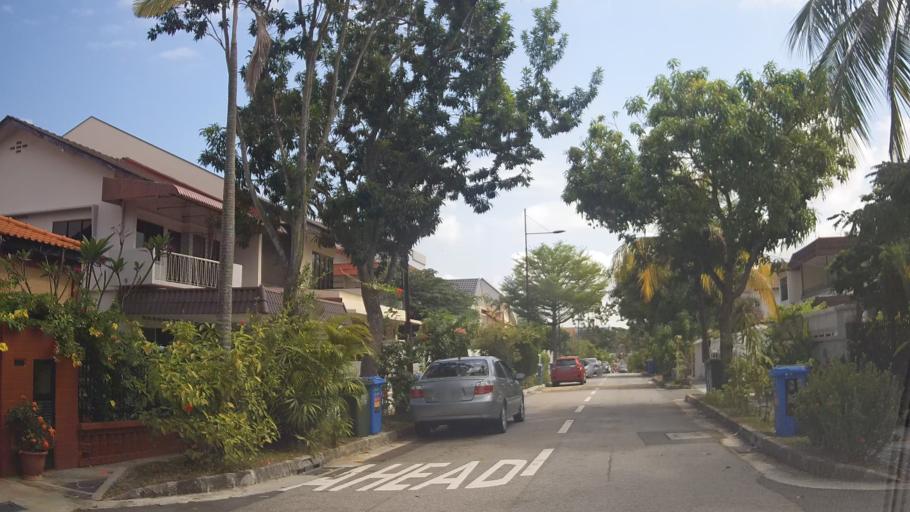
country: SG
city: Singapore
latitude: 1.3243
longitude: 103.9469
